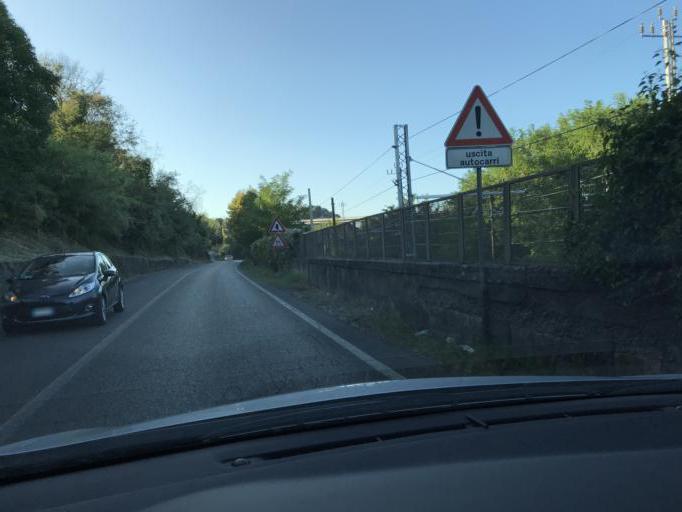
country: IT
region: Latium
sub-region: Provincia di Viterbo
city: Orte
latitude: 42.4472
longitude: 12.3931
